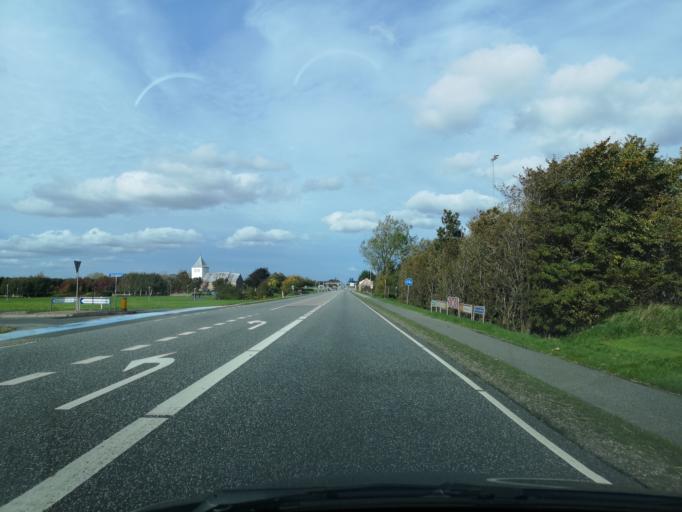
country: DK
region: Central Jutland
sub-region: Holstebro Kommune
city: Holstebro
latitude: 56.3831
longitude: 8.6130
